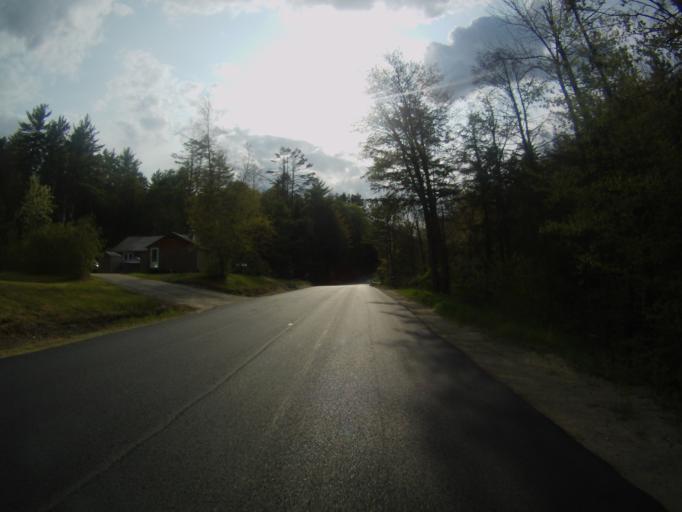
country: US
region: New York
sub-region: Warren County
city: Warrensburg
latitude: 43.8417
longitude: -73.7886
